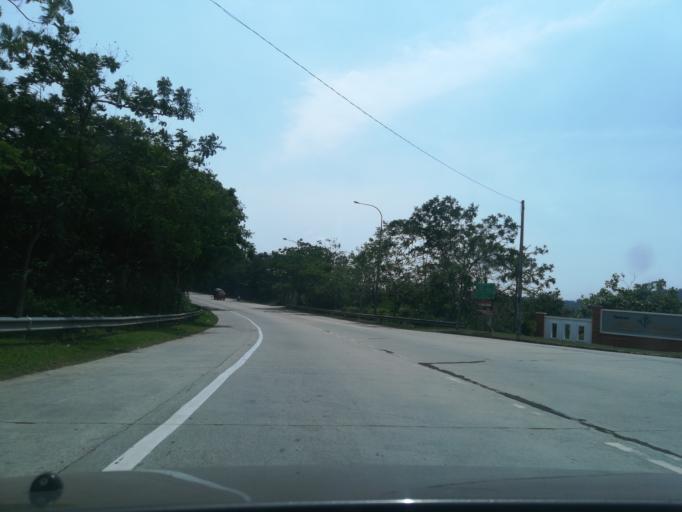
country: MY
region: Kedah
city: Kulim
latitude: 5.4145
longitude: 100.5661
